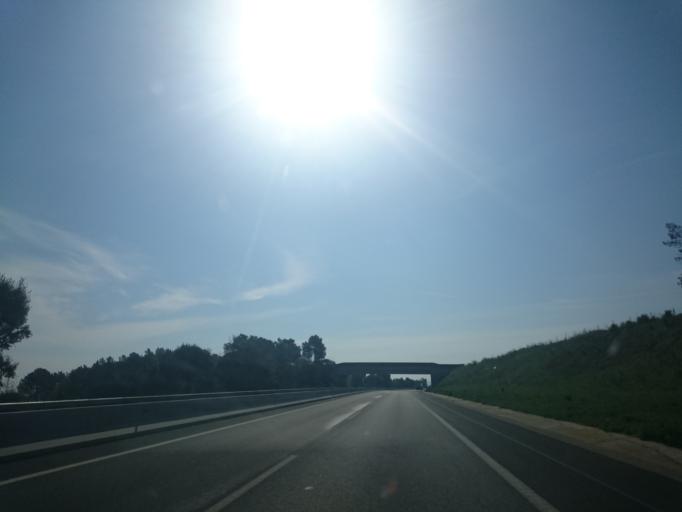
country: ES
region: Catalonia
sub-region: Provincia de Girona
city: Brunyola
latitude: 41.8884
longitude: 2.6721
